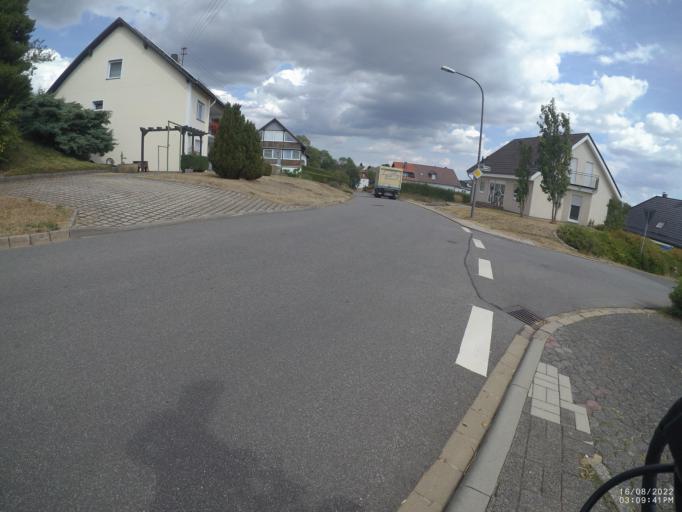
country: DE
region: Rheinland-Pfalz
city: Berndorf
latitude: 50.3061
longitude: 6.6927
